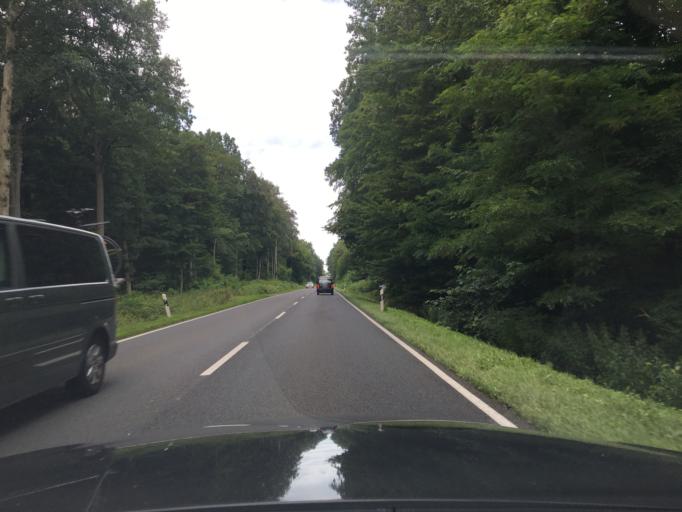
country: DE
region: Brandenburg
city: Gransee
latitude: 53.0643
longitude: 13.1857
